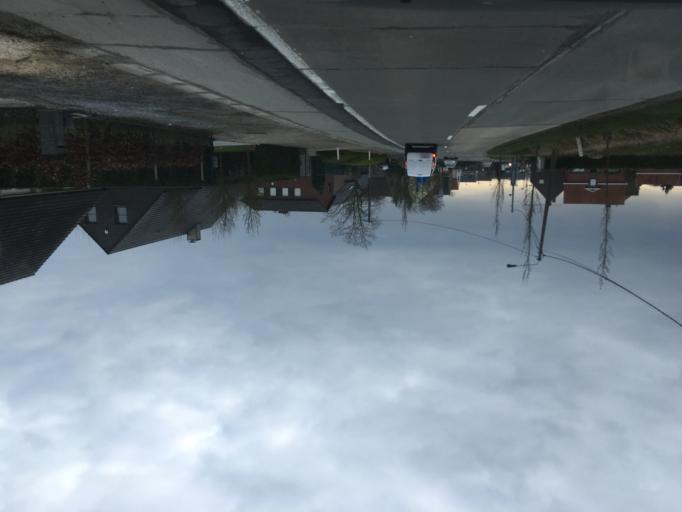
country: BE
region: Flanders
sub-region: Provincie West-Vlaanderen
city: Anzegem
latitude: 50.8455
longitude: 3.4668
